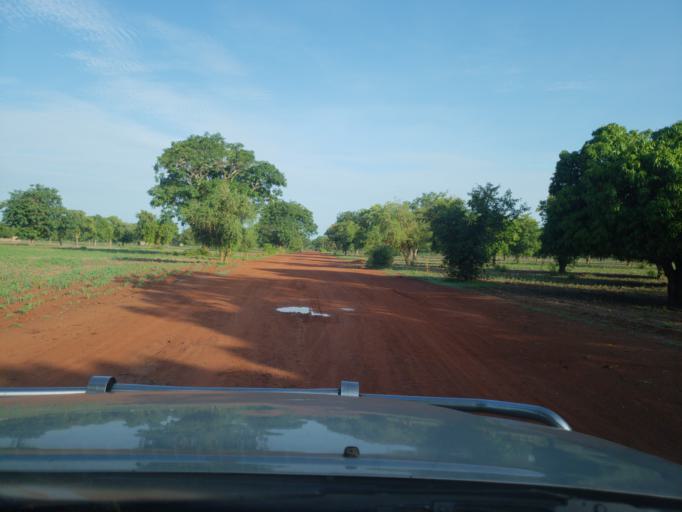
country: ML
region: Sikasso
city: Koutiala
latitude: 12.4100
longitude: -5.5534
